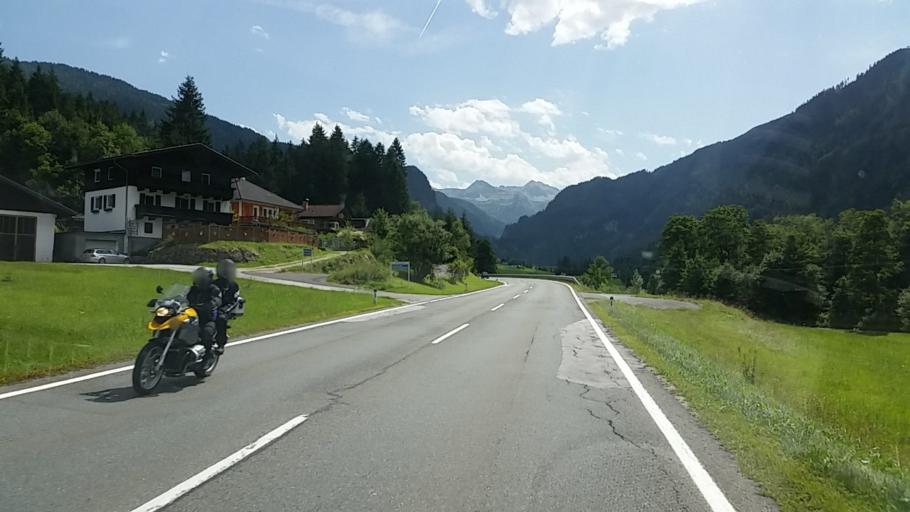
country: AT
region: Salzburg
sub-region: Politischer Bezirk Sankt Johann im Pongau
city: Untertauern
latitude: 47.3207
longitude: 13.5090
